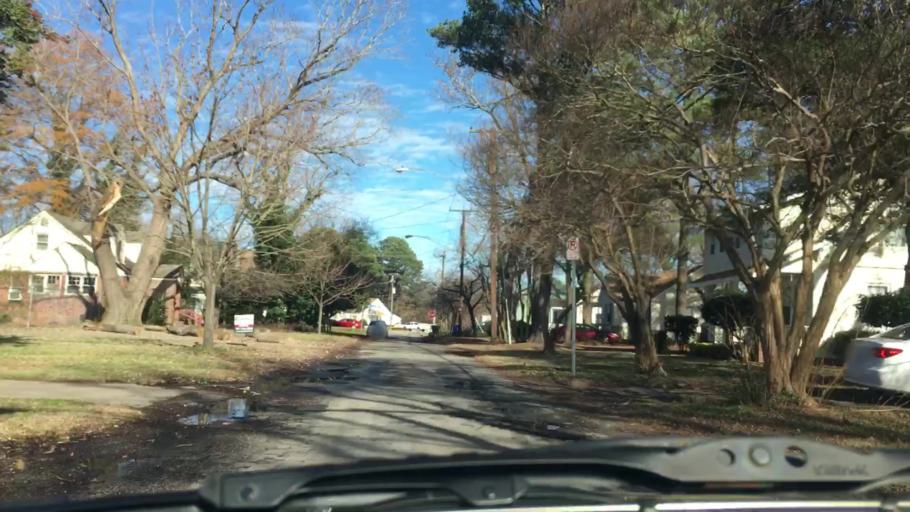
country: US
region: Virginia
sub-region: City of Norfolk
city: Norfolk
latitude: 36.8801
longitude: -76.2561
